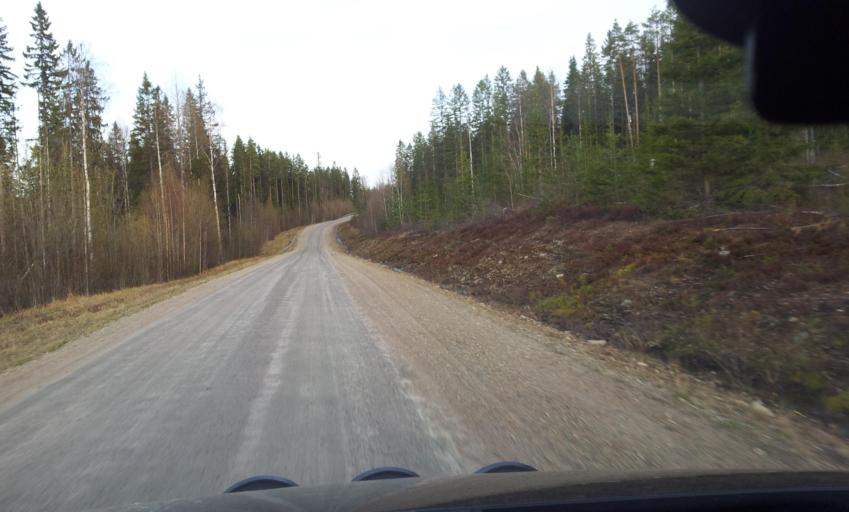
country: SE
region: Gaevleborg
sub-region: Ljusdals Kommun
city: Farila
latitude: 62.1087
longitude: 15.7244
